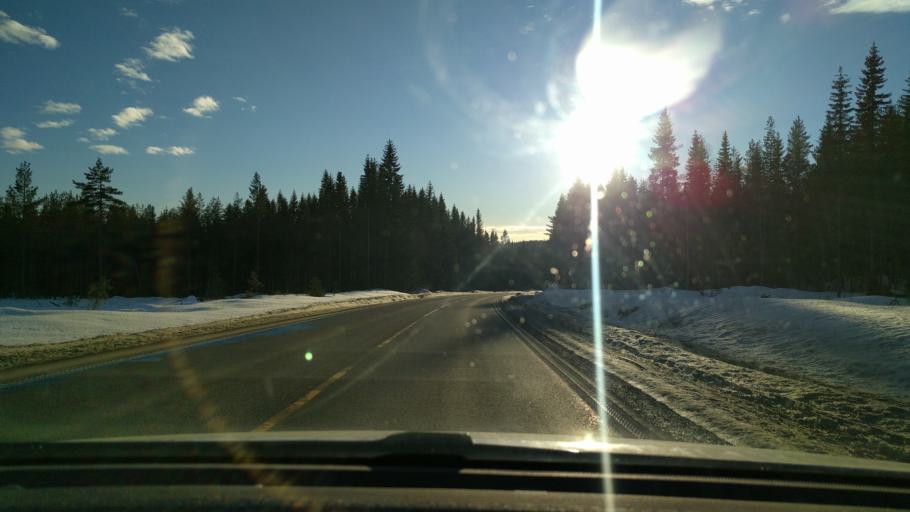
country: NO
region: Hedmark
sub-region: Elverum
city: Elverum
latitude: 61.0116
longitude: 11.8315
